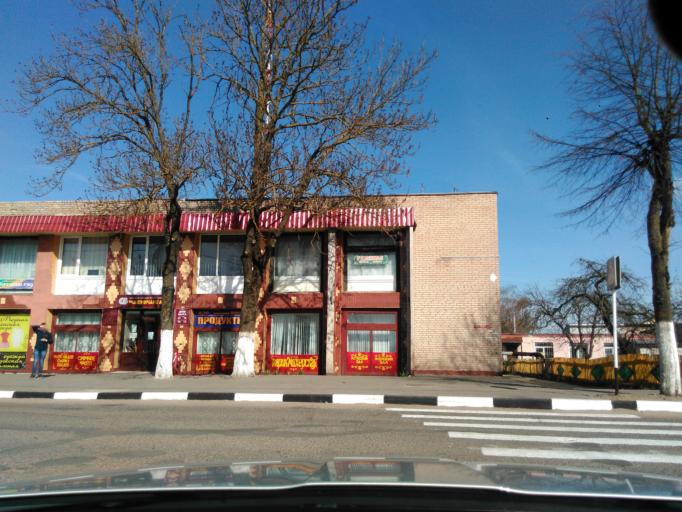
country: BY
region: Vitebsk
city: Chashniki
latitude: 54.8594
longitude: 29.1604
